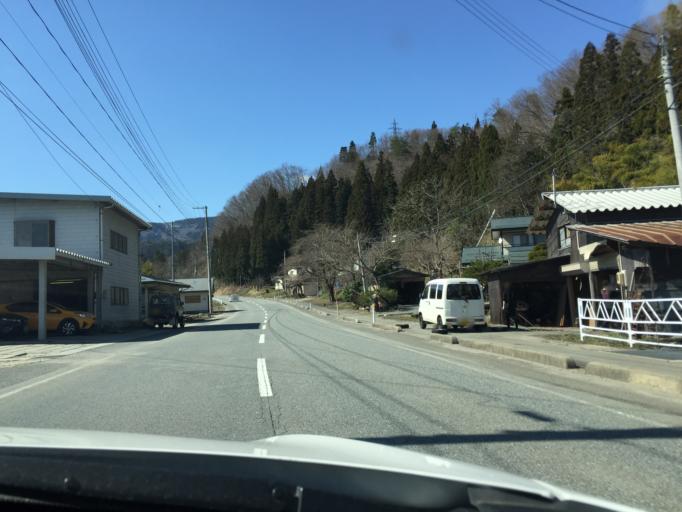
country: JP
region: Yamagata
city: Nagai
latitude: 38.2273
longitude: 140.0956
